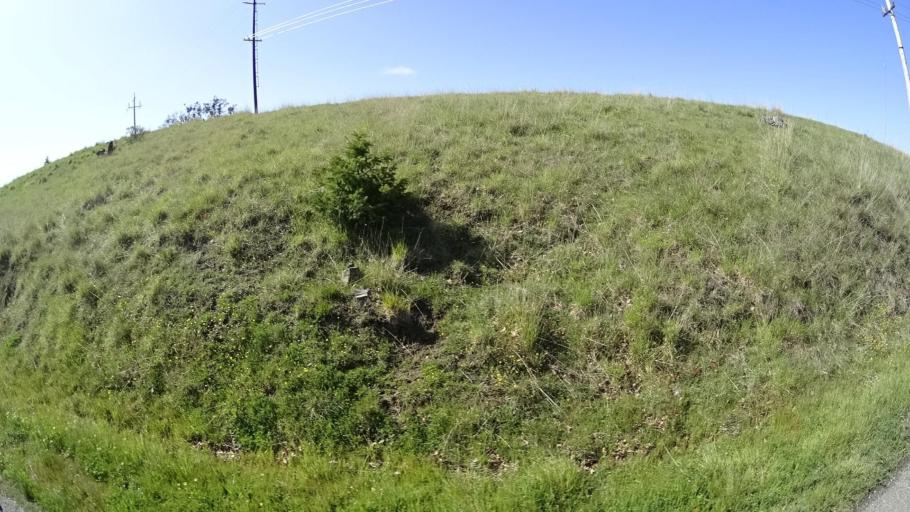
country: US
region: California
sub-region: Humboldt County
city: Redway
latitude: 40.0970
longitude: -123.6829
